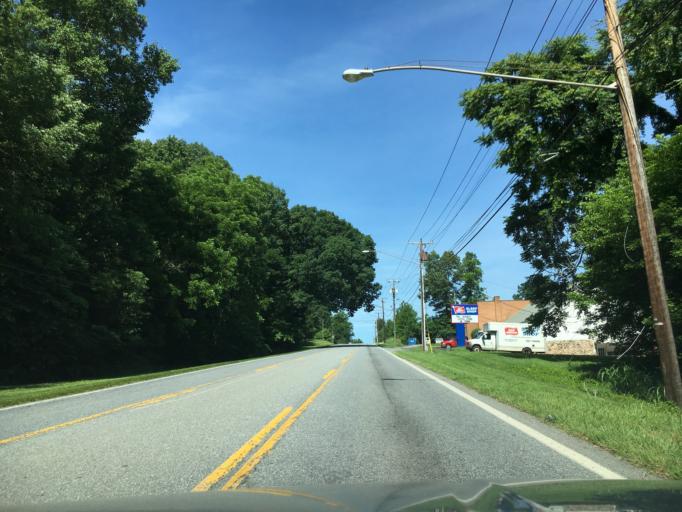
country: US
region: Virginia
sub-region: City of Lynchburg
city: West Lynchburg
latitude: 37.4017
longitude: -79.1864
